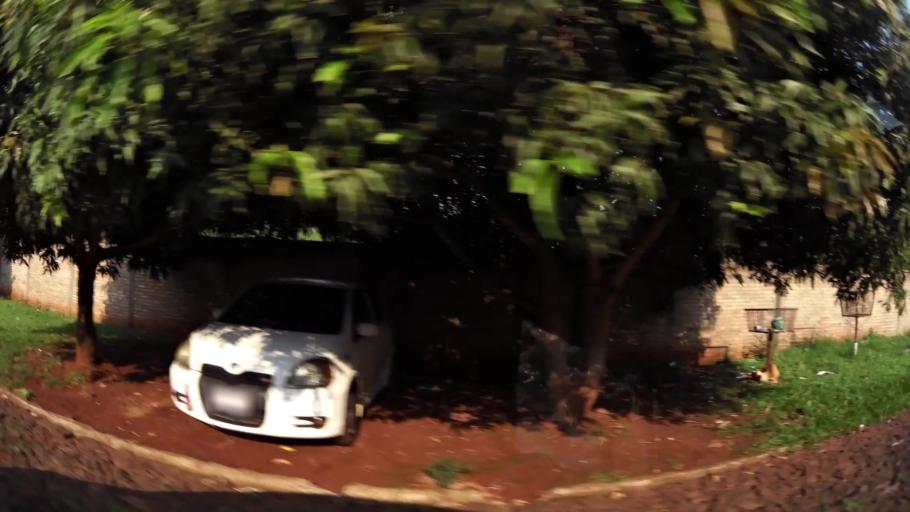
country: PY
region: Alto Parana
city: Presidente Franco
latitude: -25.5258
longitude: -54.6283
